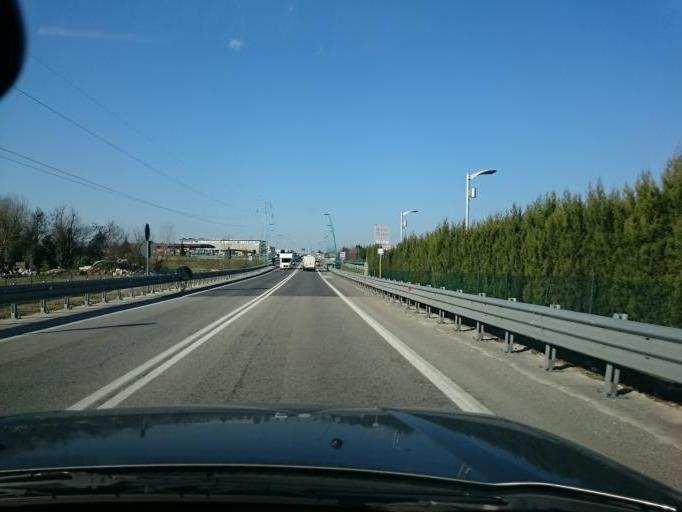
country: IT
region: Veneto
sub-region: Provincia di Verona
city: Peschiera del Garda
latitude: 45.4312
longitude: 10.6989
